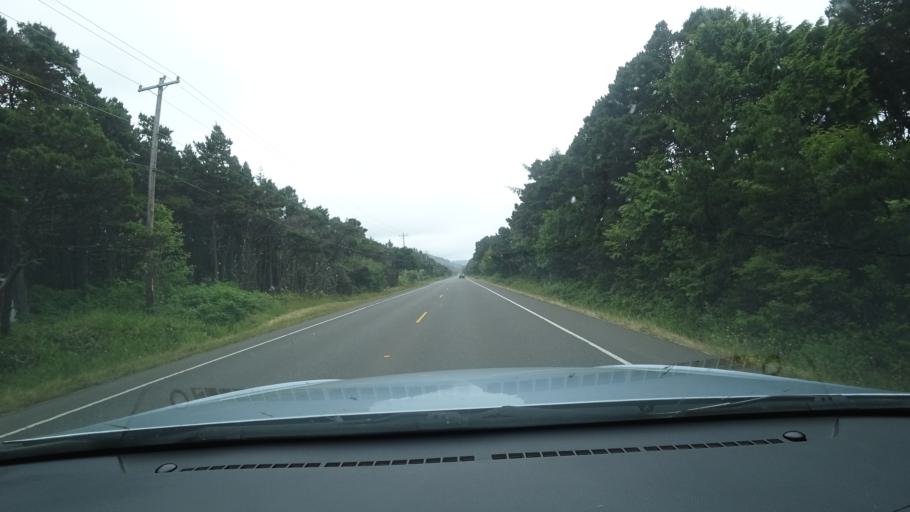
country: US
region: Oregon
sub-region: Lincoln County
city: Waldport
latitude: 44.3469
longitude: -124.0949
